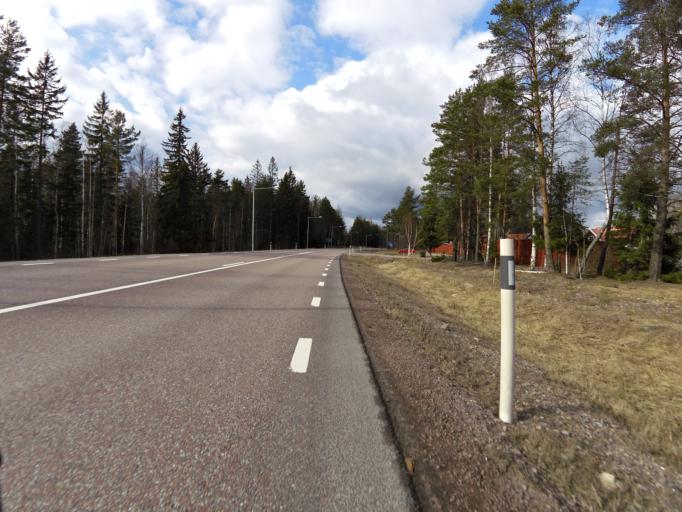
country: SE
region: Gaevleborg
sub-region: Hofors Kommun
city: Hofors
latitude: 60.4952
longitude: 16.4345
